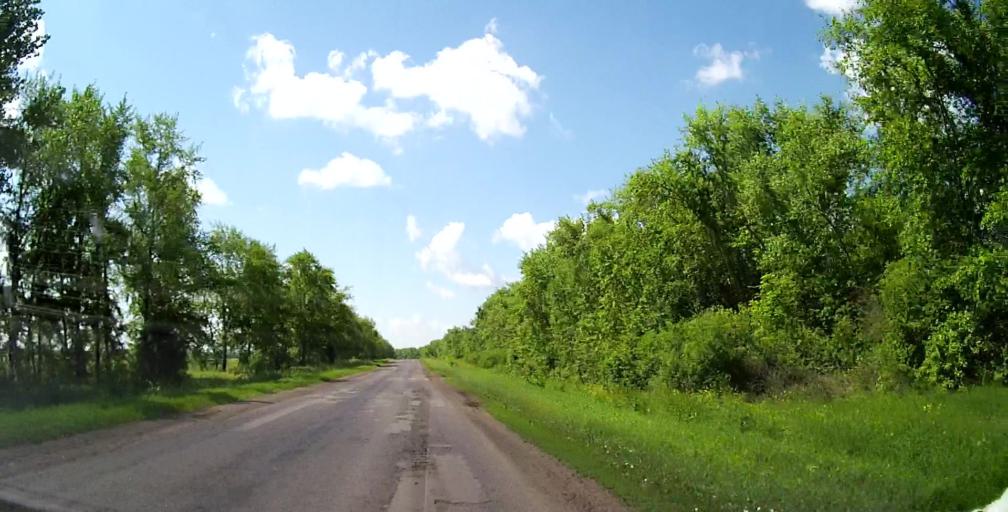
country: RU
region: Lipetsk
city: Chaplygin
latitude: 53.3134
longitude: 39.9581
